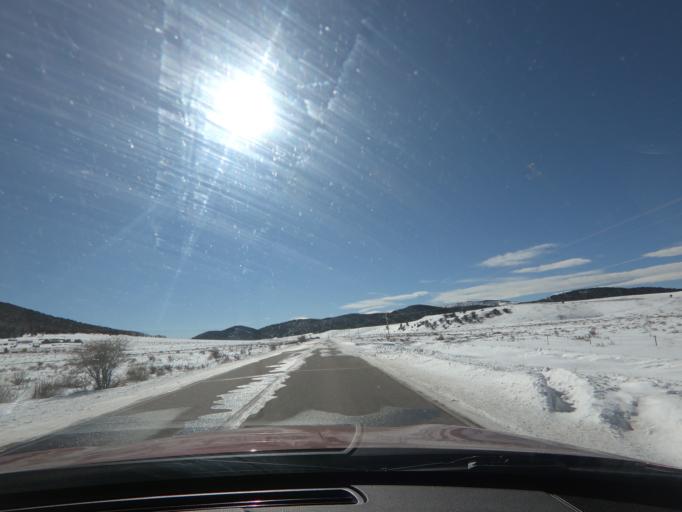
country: US
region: Colorado
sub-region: Teller County
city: Cripple Creek
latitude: 38.7787
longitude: -105.1216
